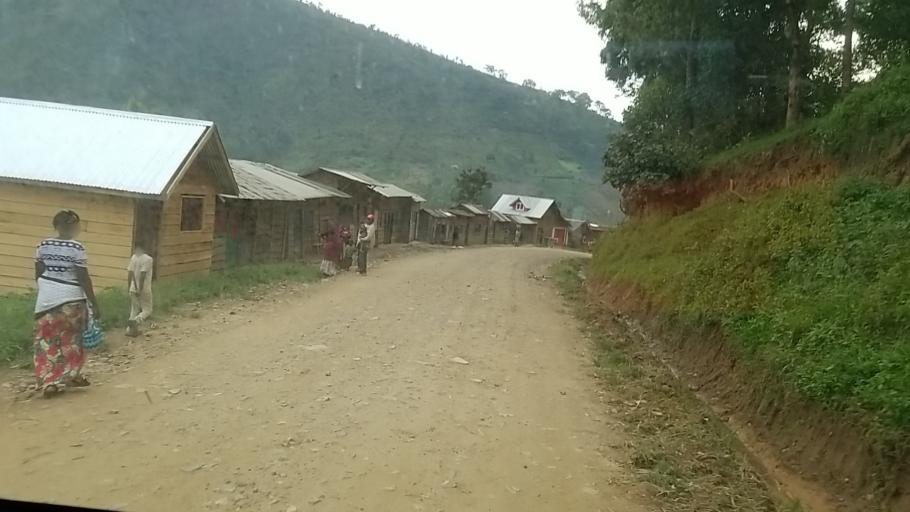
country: CD
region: Nord Kivu
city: Sake
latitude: -1.9593
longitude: 28.9219
